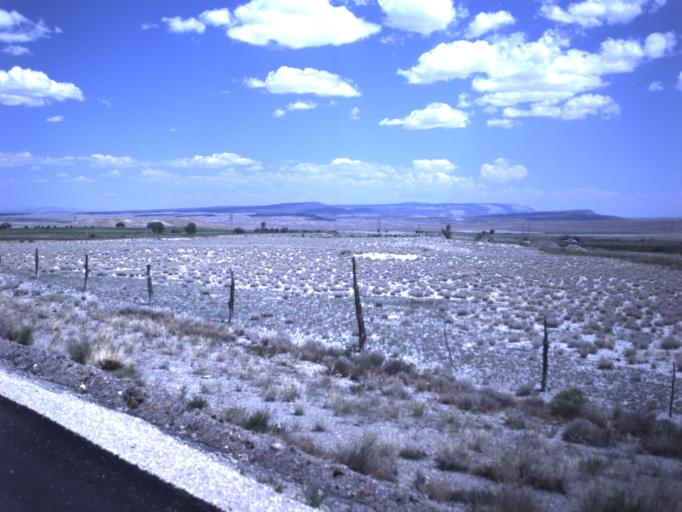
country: US
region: Utah
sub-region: Emery County
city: Castle Dale
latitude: 39.2431
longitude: -110.9943
